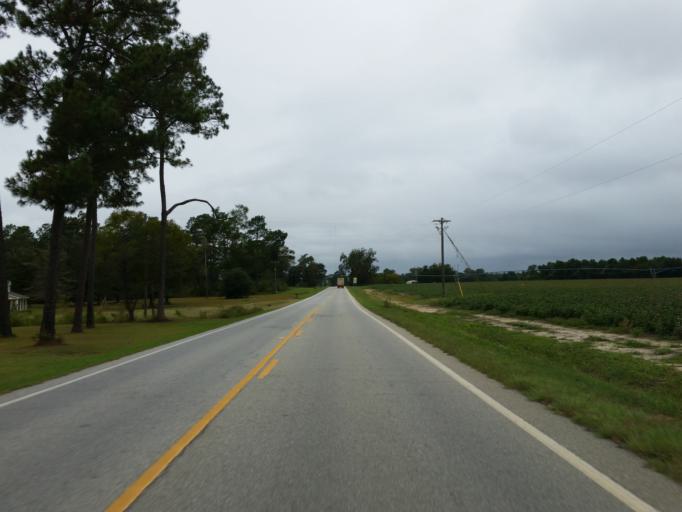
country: US
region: Georgia
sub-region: Cook County
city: Adel
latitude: 31.1336
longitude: -83.3775
